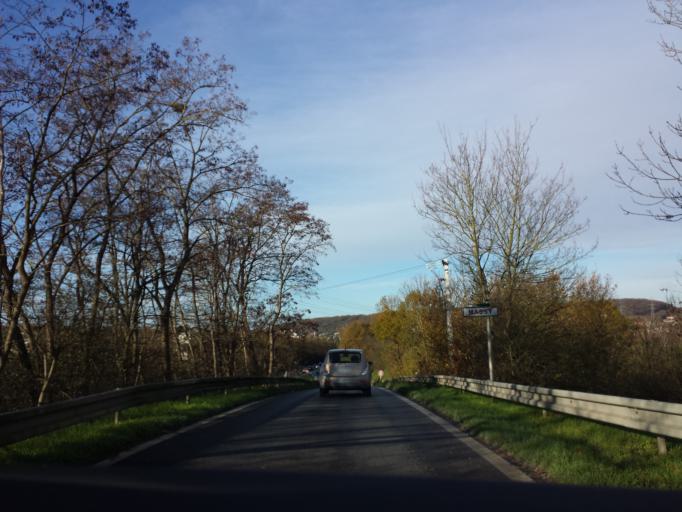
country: FR
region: Ile-de-France
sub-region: Departement de l'Essonne
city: Palaiseau
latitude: 48.7312
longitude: 2.2411
